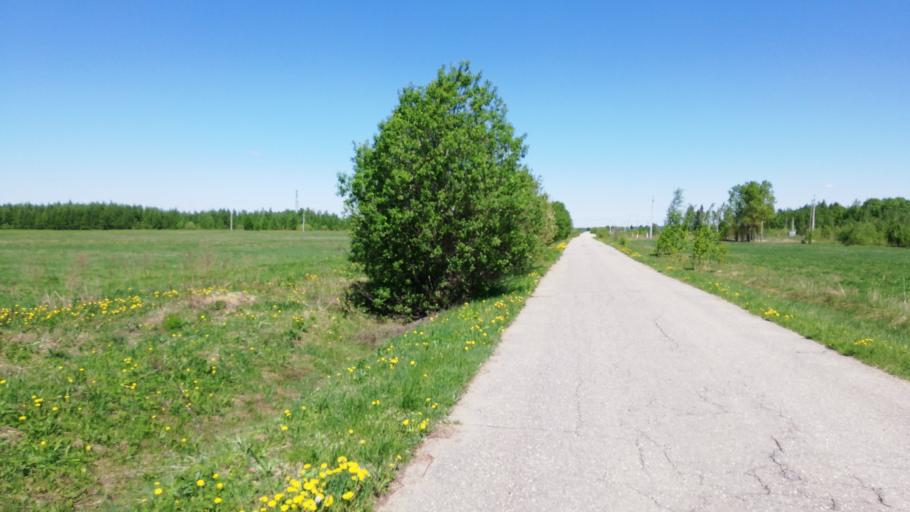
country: RU
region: Ivanovo
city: Pistsovo
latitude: 57.1221
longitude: 40.5993
